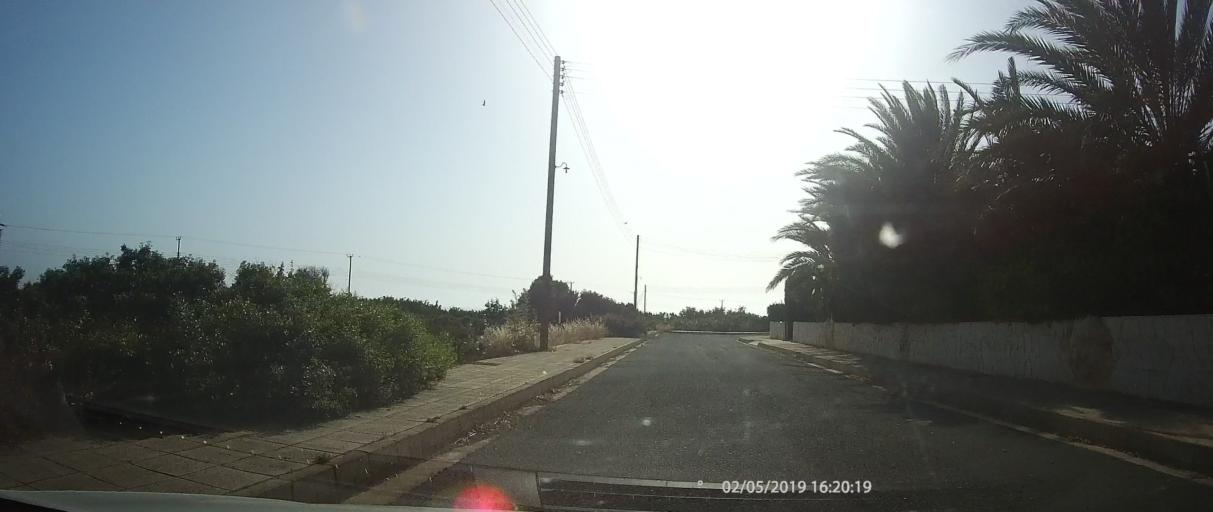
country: CY
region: Pafos
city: Pegeia
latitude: 34.8866
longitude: 32.3359
